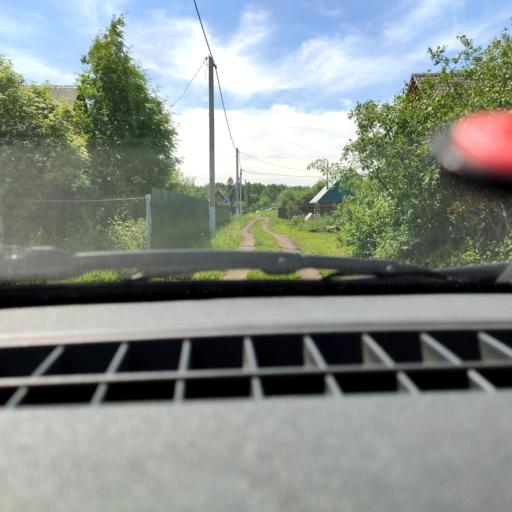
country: RU
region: Bashkortostan
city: Kabakovo
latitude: 54.7248
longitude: 56.2050
